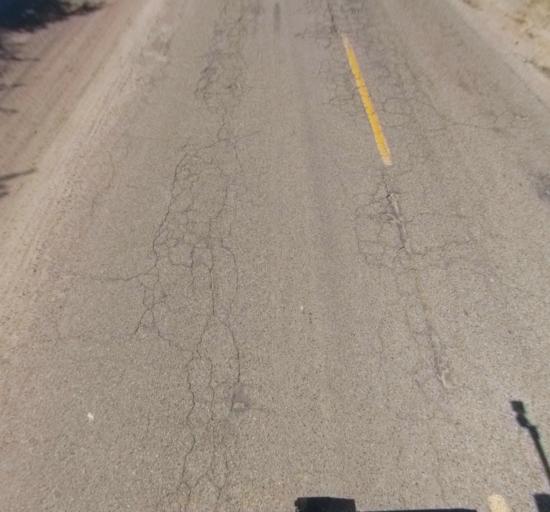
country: US
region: California
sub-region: Madera County
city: Madera
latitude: 36.9478
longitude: -120.1560
